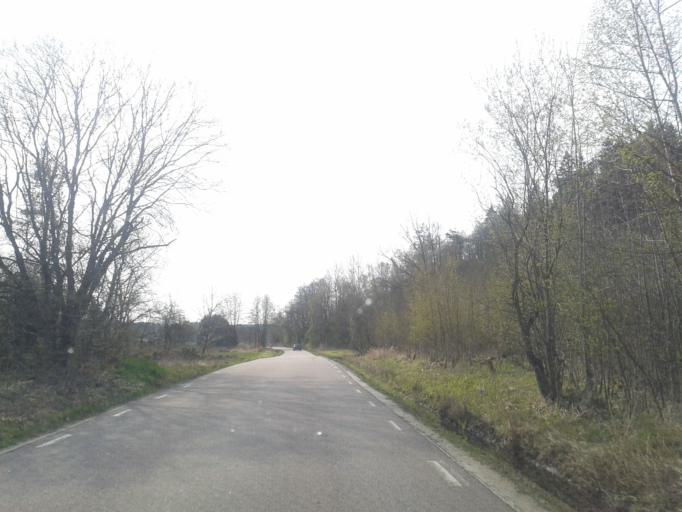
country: SE
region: Vaestra Goetaland
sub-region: Kungalvs Kommun
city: Kode
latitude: 57.9074
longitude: 11.8928
